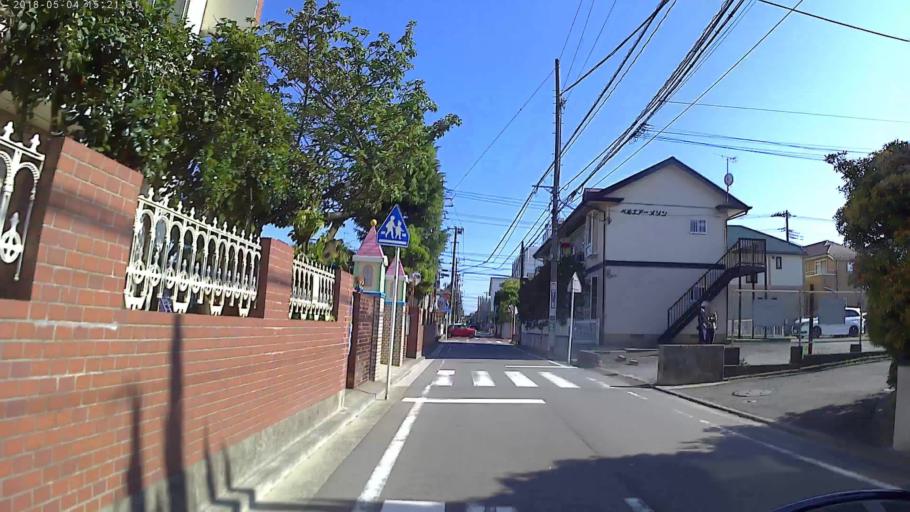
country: JP
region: Kanagawa
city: Yokohama
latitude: 35.5393
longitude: 139.6196
